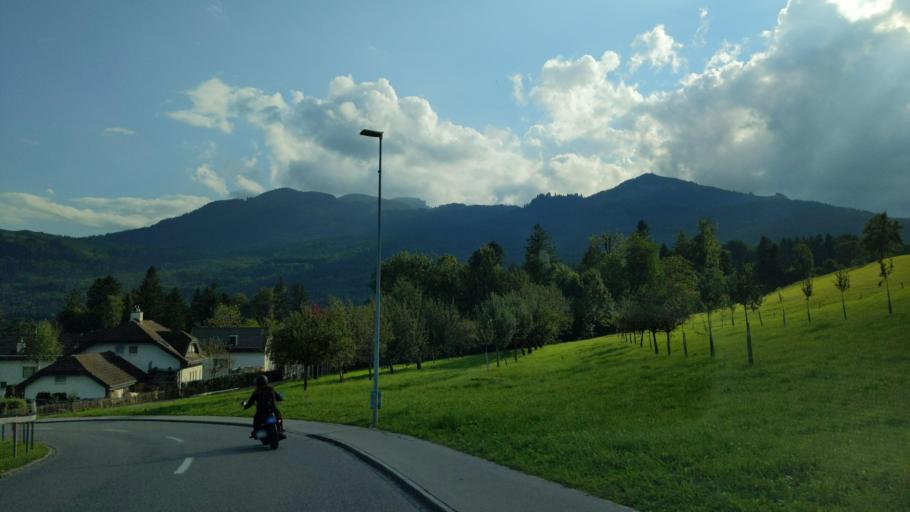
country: CH
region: Saint Gallen
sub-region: Wahlkreis Rheintal
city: Eichberg
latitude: 47.3448
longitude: 9.5263
